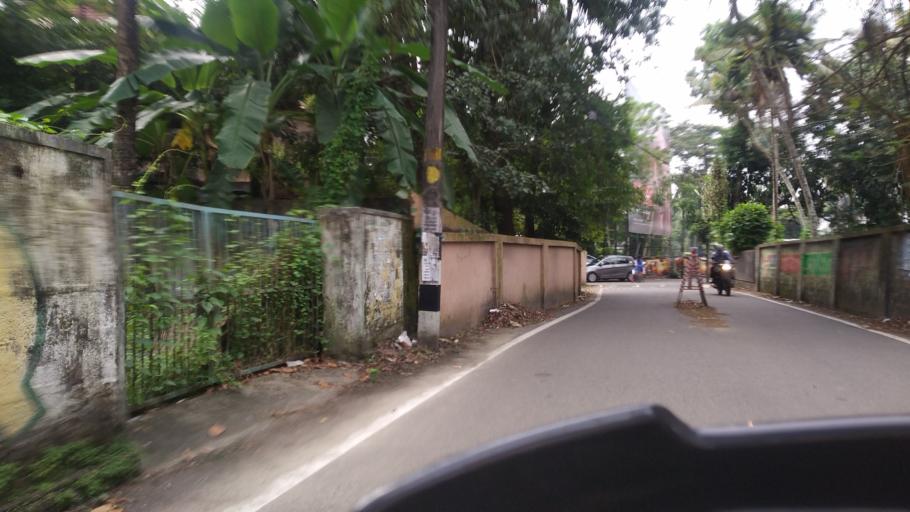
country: IN
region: Kerala
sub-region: Thrissur District
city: Kodungallur
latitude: 10.1416
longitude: 76.2331
